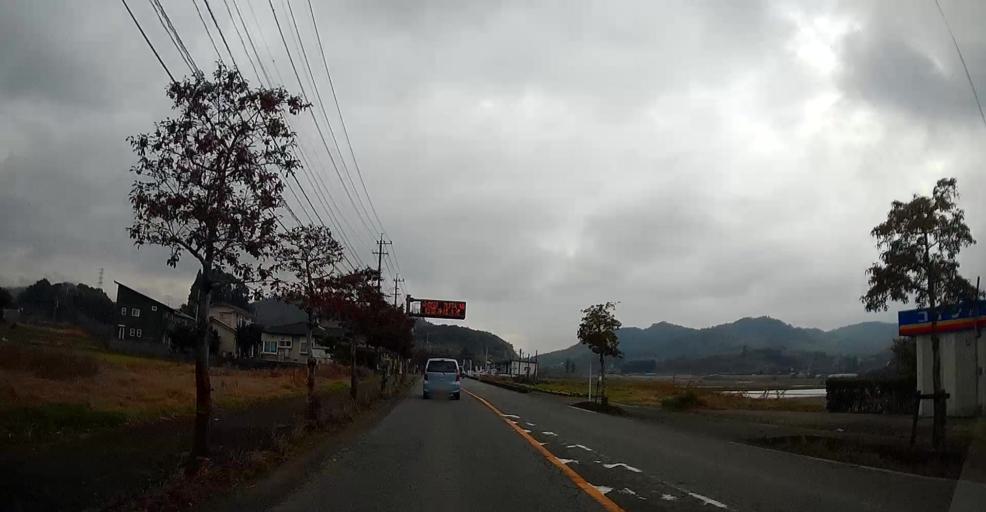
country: JP
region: Kumamoto
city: Matsubase
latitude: 32.6491
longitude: 130.7172
